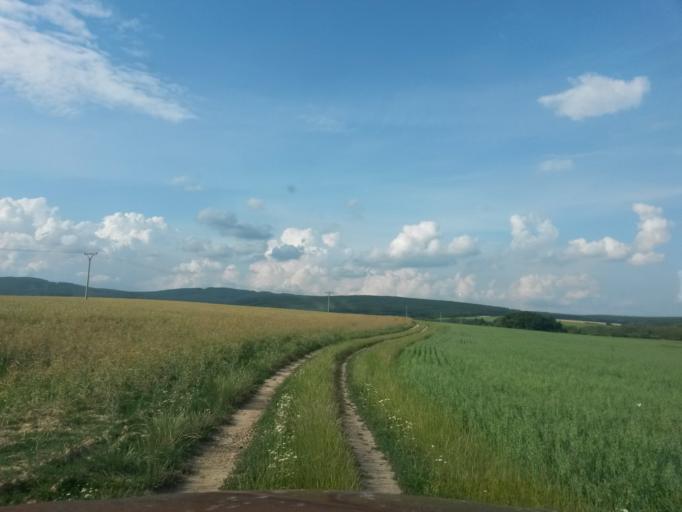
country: SK
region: Kosicky
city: Moldava nad Bodvou
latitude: 48.6557
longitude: 21.1076
